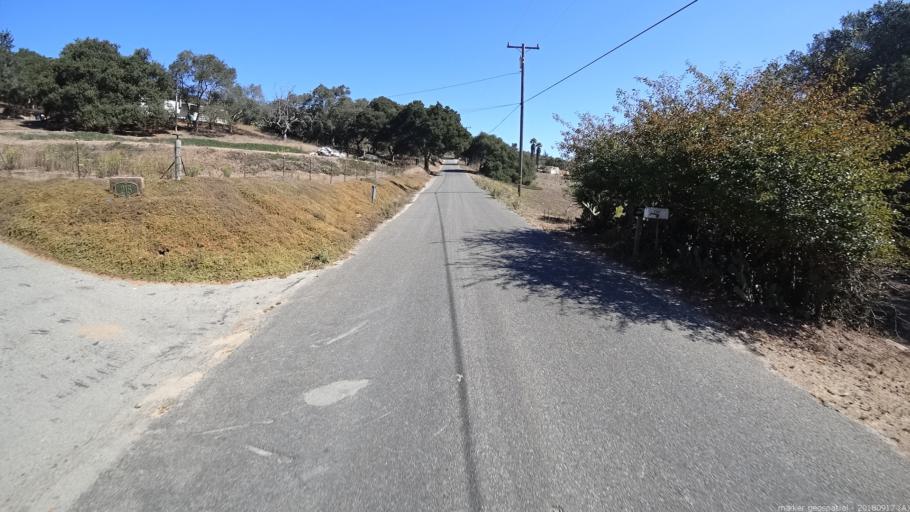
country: US
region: California
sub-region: Monterey County
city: Elkhorn
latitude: 36.8284
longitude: -121.6975
